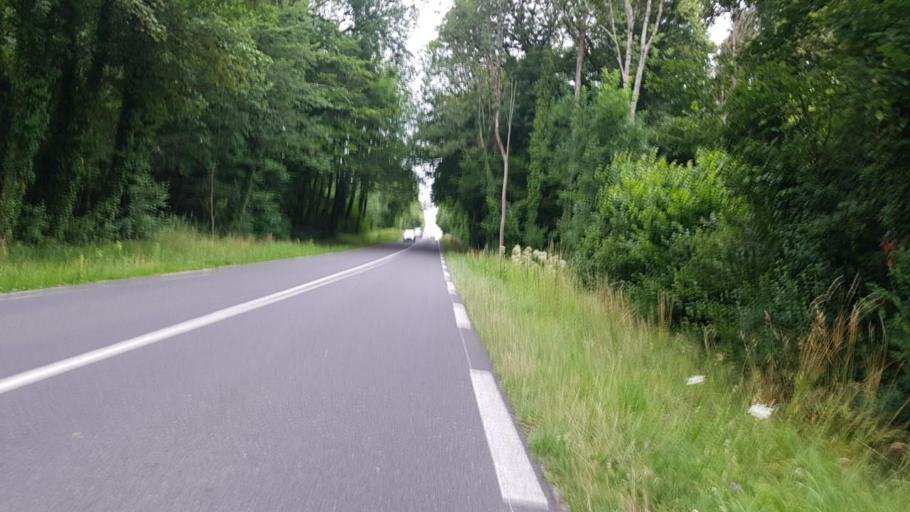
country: FR
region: Champagne-Ardenne
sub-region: Departement de la Marne
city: Sermaize-les-Bains
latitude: 48.7755
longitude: 4.8759
